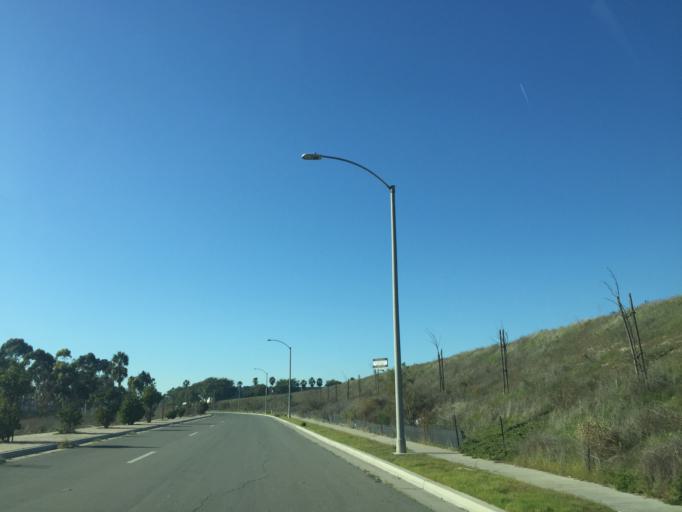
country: MX
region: Baja California
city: Tijuana
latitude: 32.5566
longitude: -116.9245
